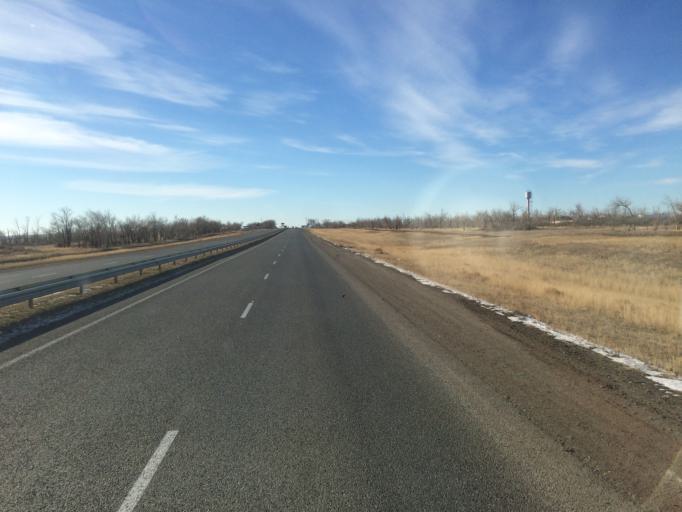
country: KZ
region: Aqtoebe
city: Aqtobe
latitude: 50.2662
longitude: 56.9632
